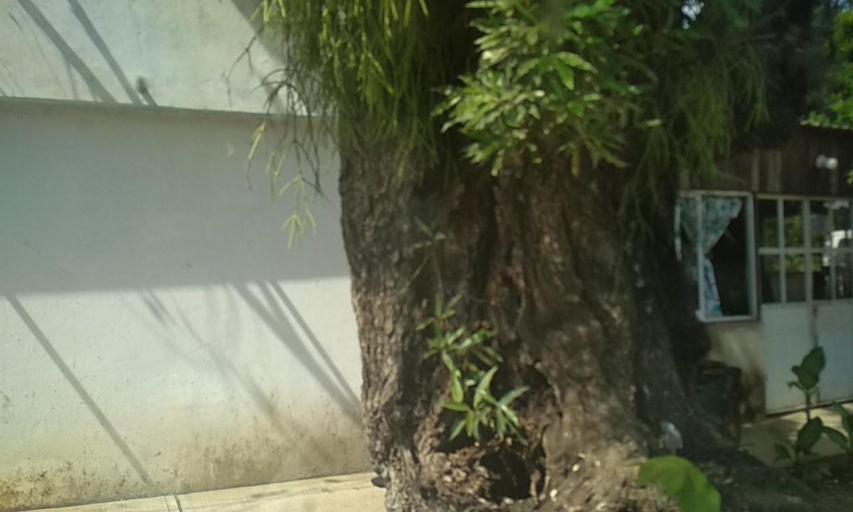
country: MX
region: Veracruz
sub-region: Martinez de la Torre
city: La Union Paso Largo
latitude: 20.1304
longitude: -96.9966
